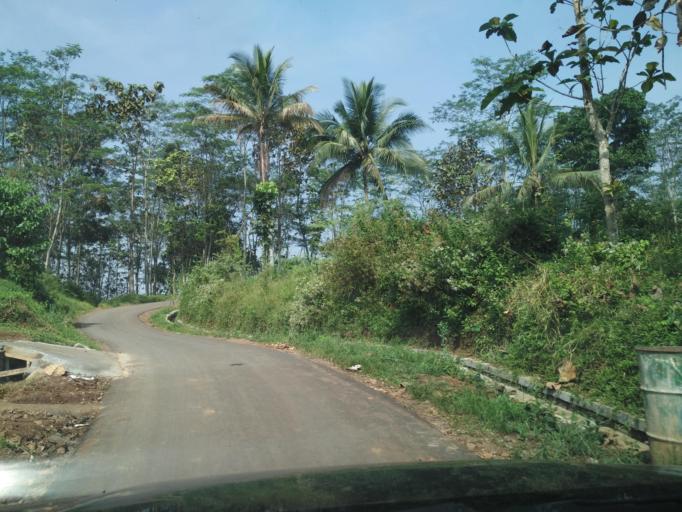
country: ID
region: West Java
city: Ciranjang-hilir
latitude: -6.7959
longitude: 107.1468
